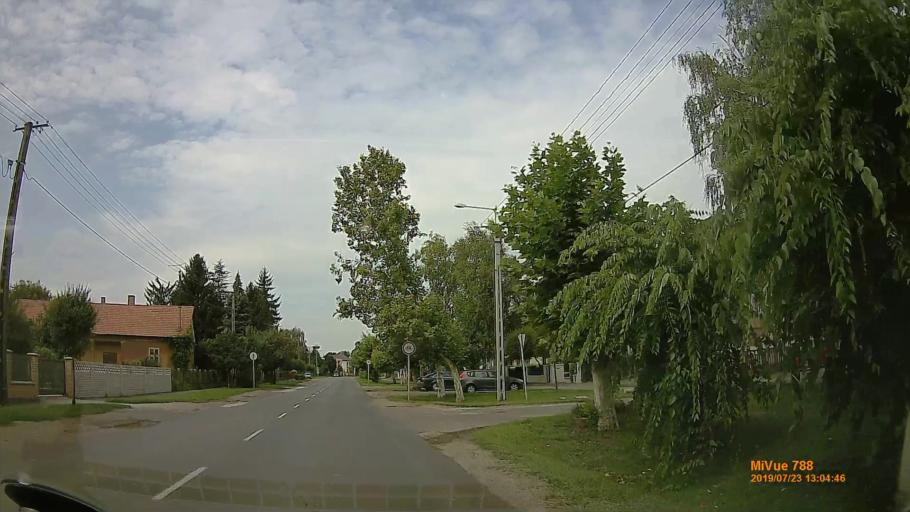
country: HU
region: Szabolcs-Szatmar-Bereg
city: Tiszavasvari
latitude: 47.9528
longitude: 21.3644
